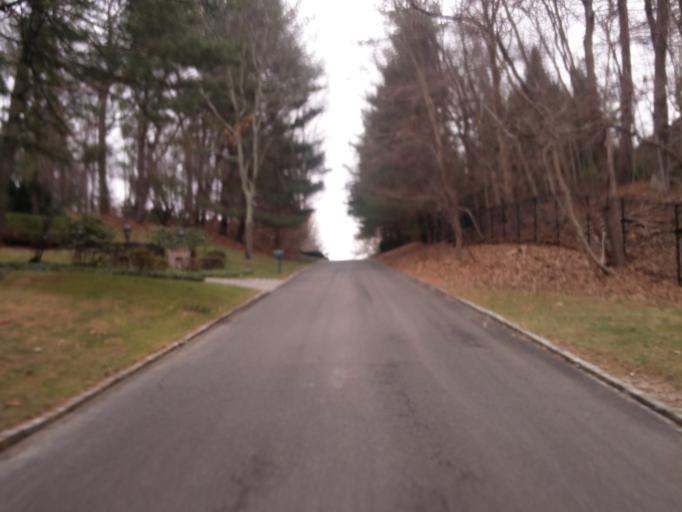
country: US
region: New York
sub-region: Nassau County
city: Upper Brookville
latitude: 40.8659
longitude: -73.5658
